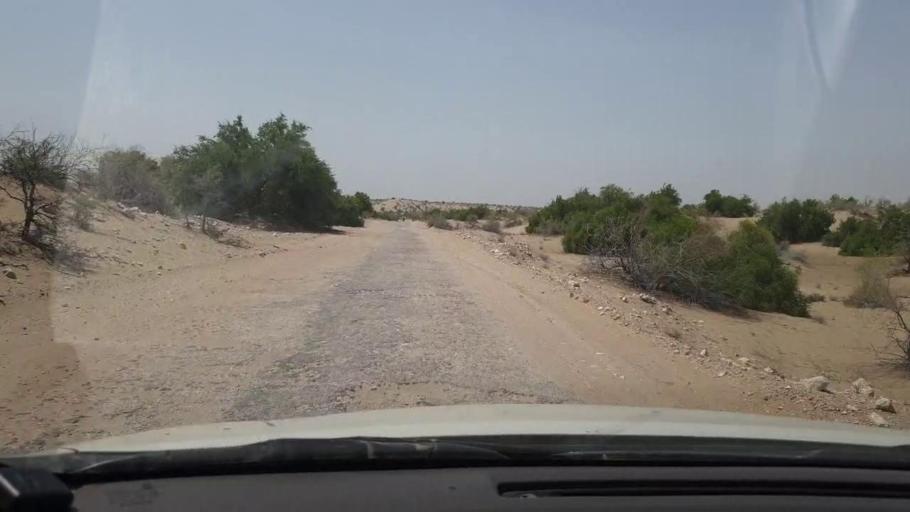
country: PK
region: Sindh
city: Rohri
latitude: 27.3107
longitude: 69.2816
